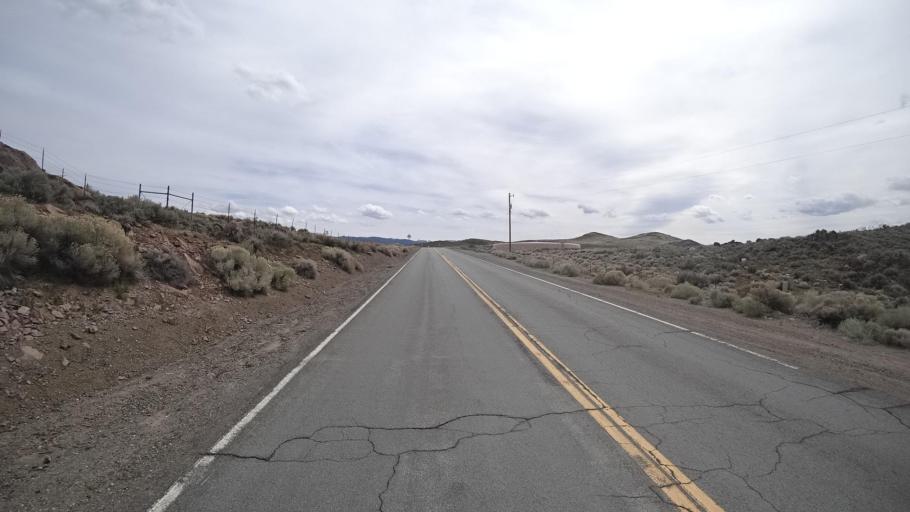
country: US
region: Nevada
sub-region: Washoe County
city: Sparks
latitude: 39.4687
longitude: -119.7547
